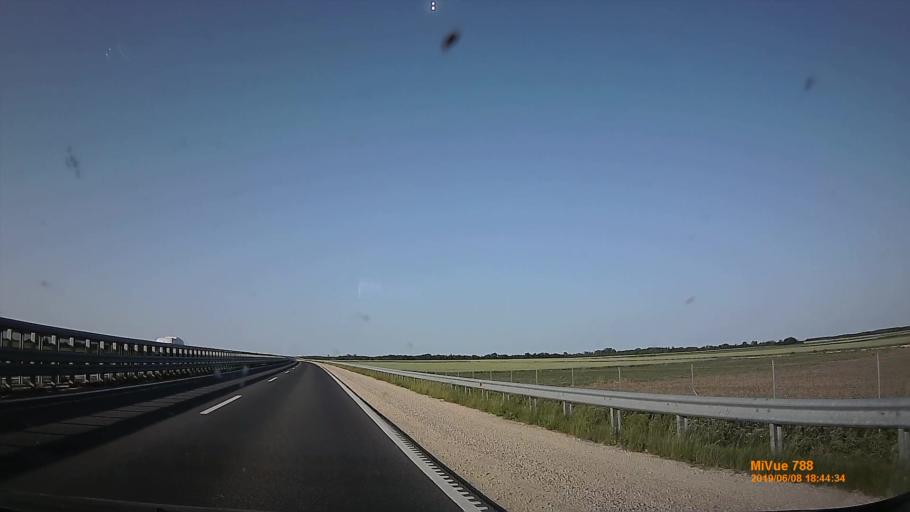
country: HU
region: Gyor-Moson-Sopron
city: Beled
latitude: 47.4678
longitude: 17.1297
